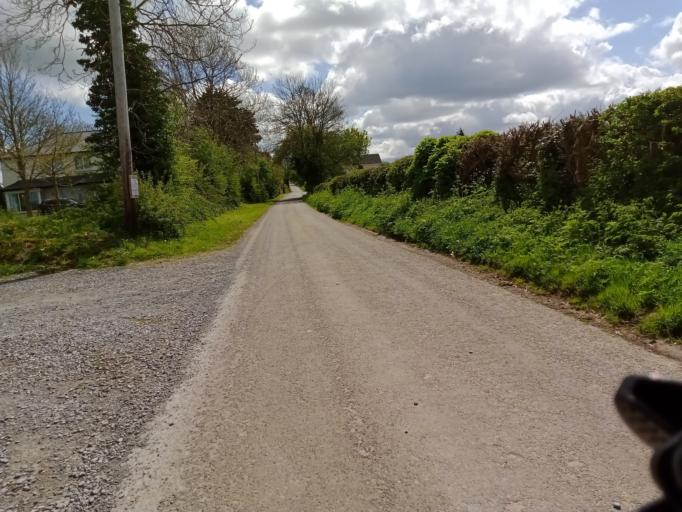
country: IE
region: Leinster
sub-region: Kilkenny
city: Thomastown
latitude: 52.5832
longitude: -7.1349
